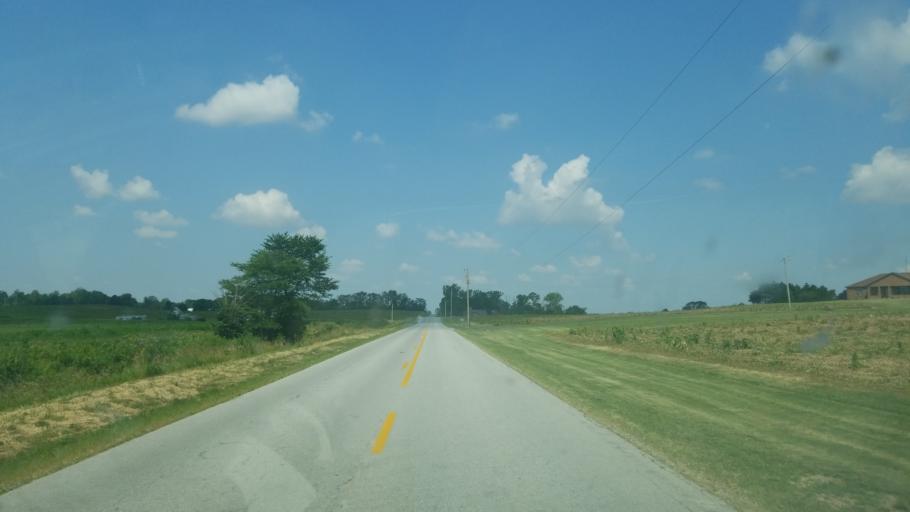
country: US
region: Ohio
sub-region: Auglaize County
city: Cridersville
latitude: 40.5709
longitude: -84.0911
